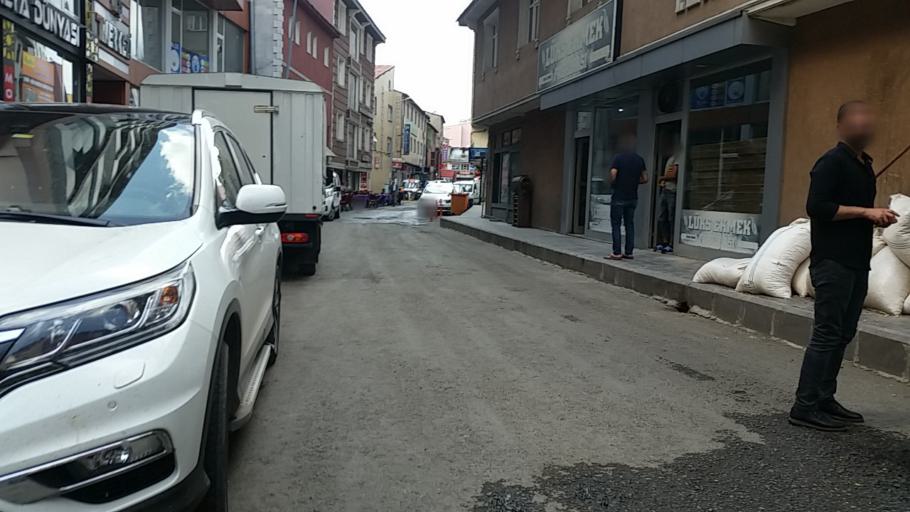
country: TR
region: Agri
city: Agri
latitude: 39.7205
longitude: 43.0536
